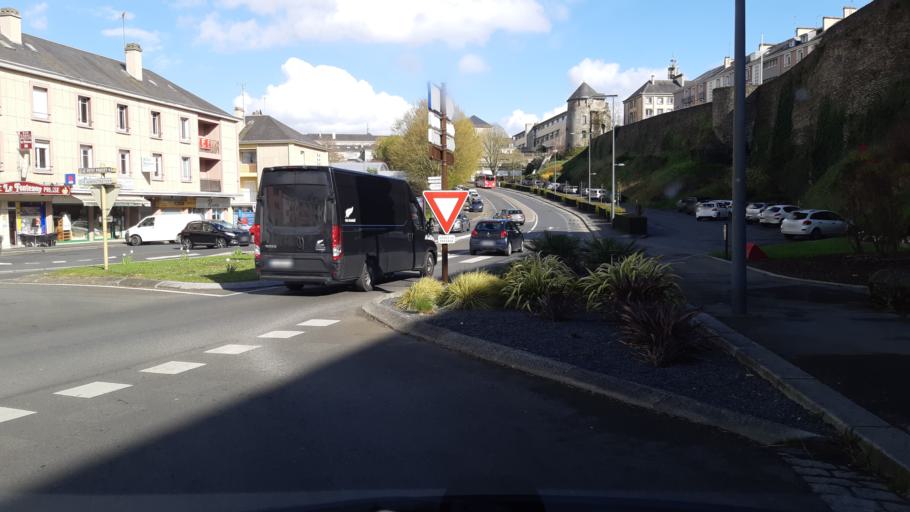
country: FR
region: Lower Normandy
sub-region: Departement de la Manche
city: Saint-Lo
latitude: 49.1166
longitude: -1.0946
